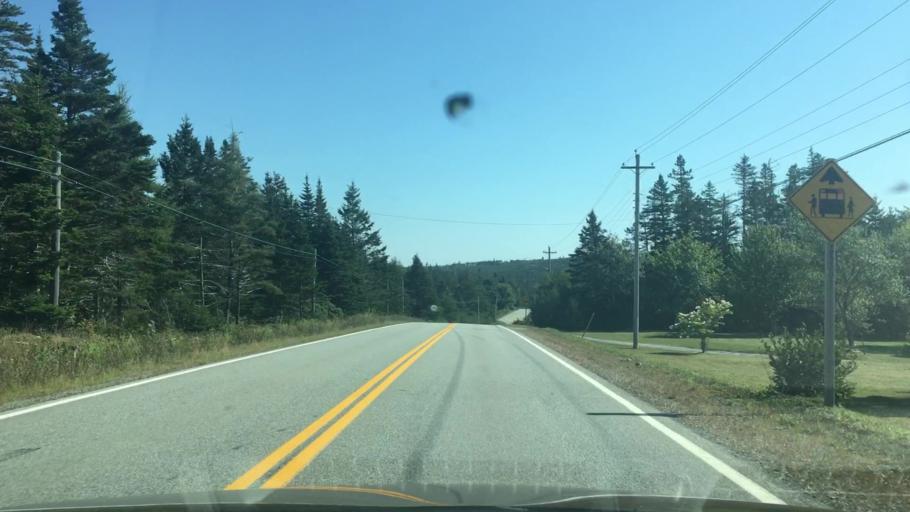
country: CA
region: Nova Scotia
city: New Glasgow
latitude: 44.8087
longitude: -62.6867
